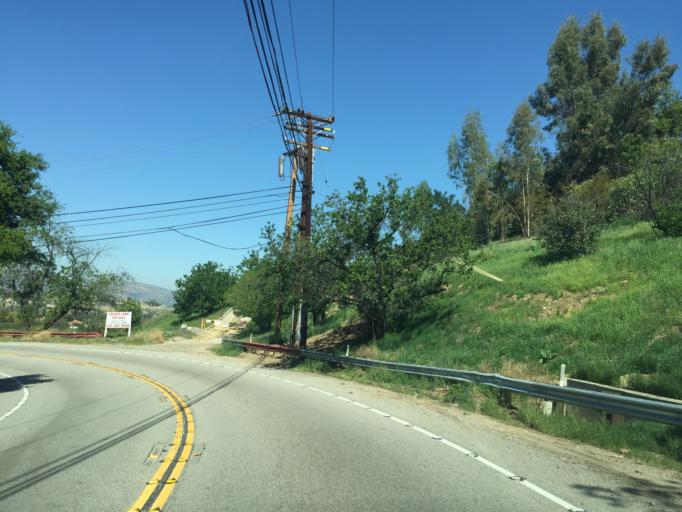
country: US
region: California
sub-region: Los Angeles County
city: Woodland Hills
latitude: 34.1443
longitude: -118.6043
